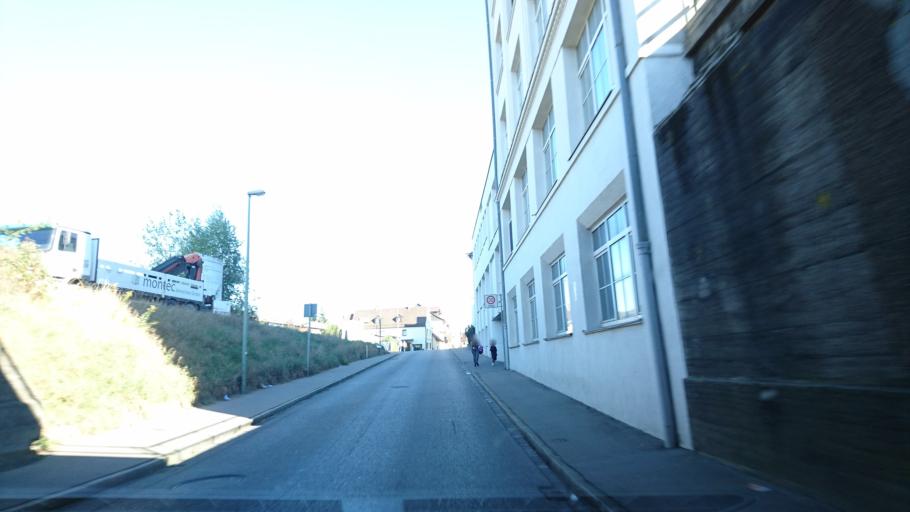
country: DE
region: Bavaria
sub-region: Swabia
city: Augsburg
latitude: 48.3858
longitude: 10.8710
